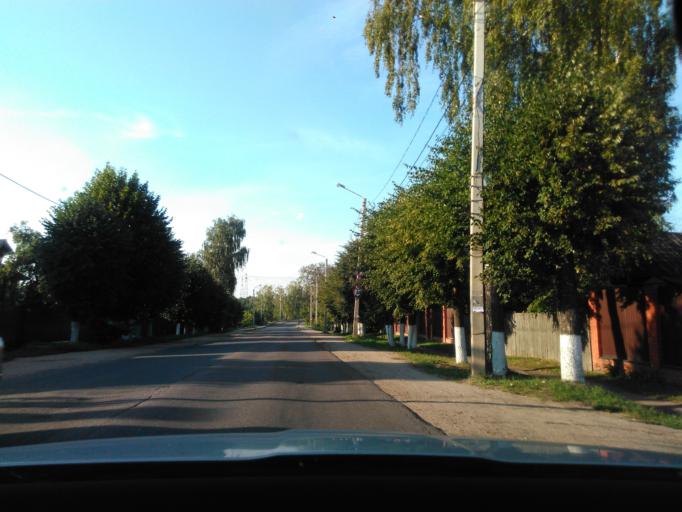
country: RU
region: Tverskaya
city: Konakovo
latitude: 56.7056
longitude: 36.7694
